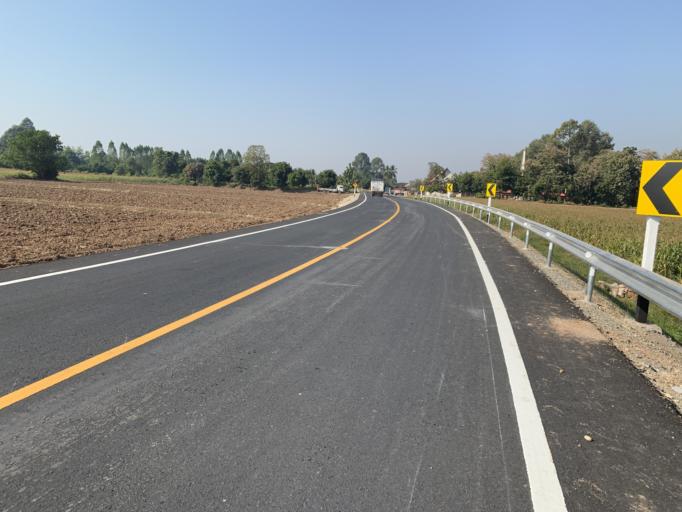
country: TH
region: Uttaradit
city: Phichai
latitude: 17.3518
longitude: 100.0714
